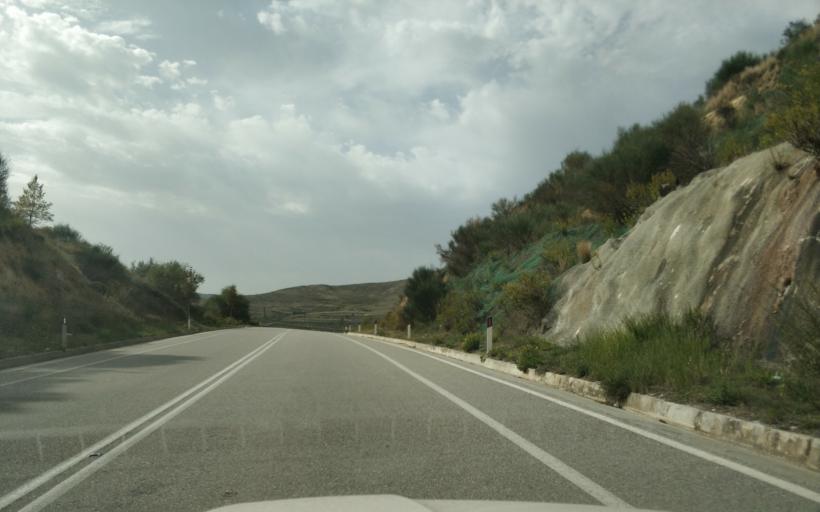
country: AL
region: Gjirokaster
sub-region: Rrethi i Tepelenes
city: Krahes
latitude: 40.3982
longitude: 19.8675
